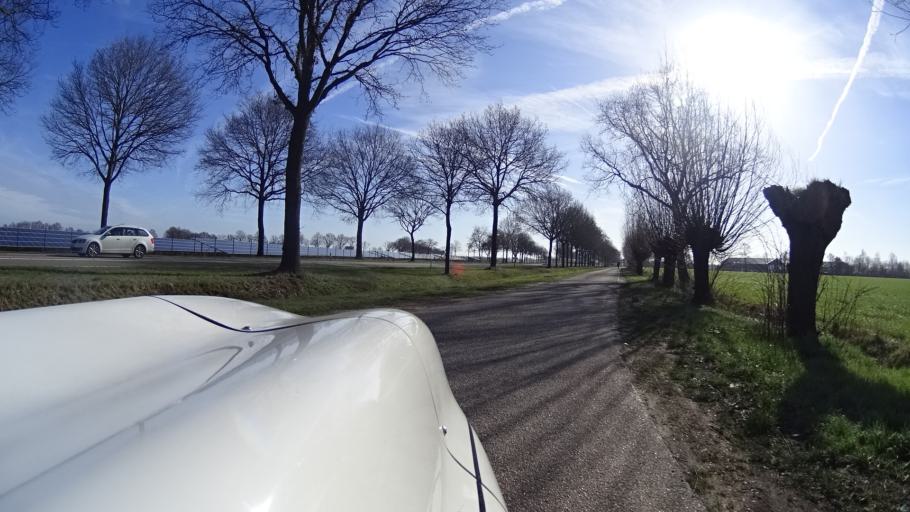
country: NL
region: North Brabant
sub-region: Gemeente Uden
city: Volkel
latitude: 51.6481
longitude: 5.6684
